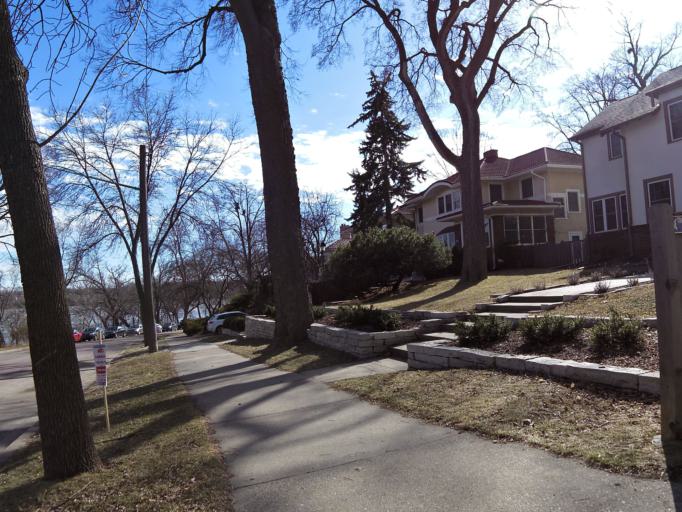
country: US
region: Minnesota
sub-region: Hennepin County
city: Saint Louis Park
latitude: 44.9240
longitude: -93.3113
